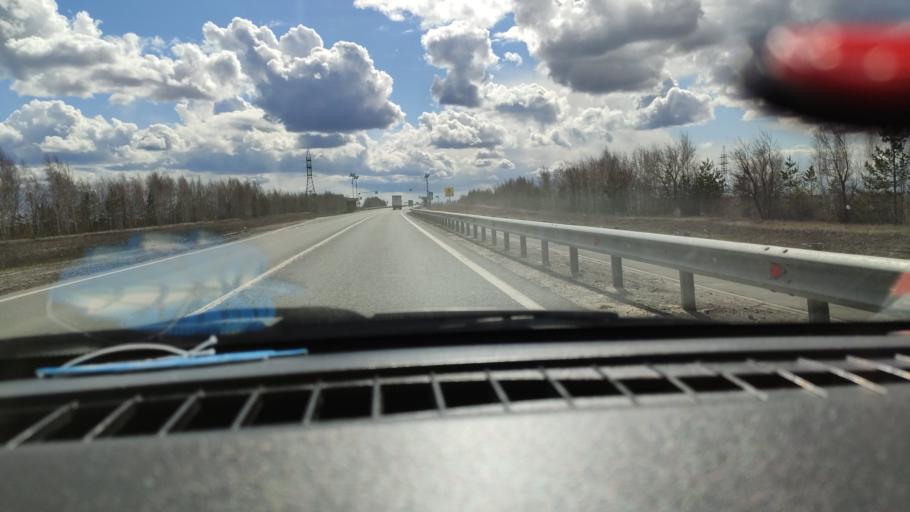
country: RU
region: Saratov
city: Dukhovnitskoye
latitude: 52.8390
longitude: 48.2451
